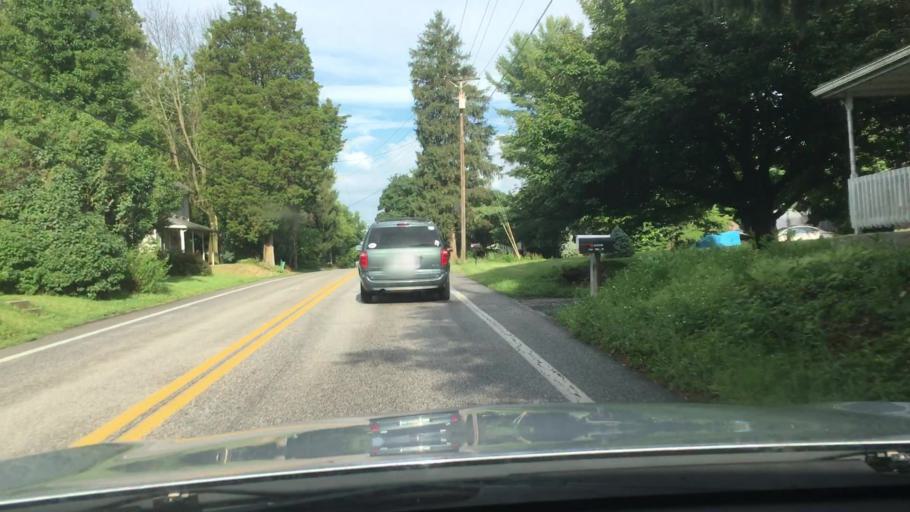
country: US
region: Pennsylvania
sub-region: York County
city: Dillsburg
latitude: 40.1488
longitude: -77.0703
